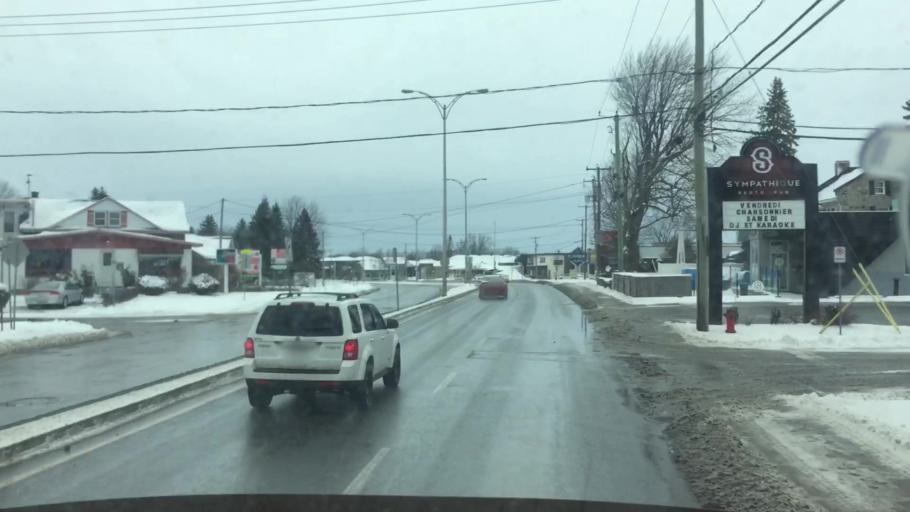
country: CA
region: Quebec
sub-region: Monteregie
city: Saint-Jean-sur-Richelieu
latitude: 45.3599
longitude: -73.3017
